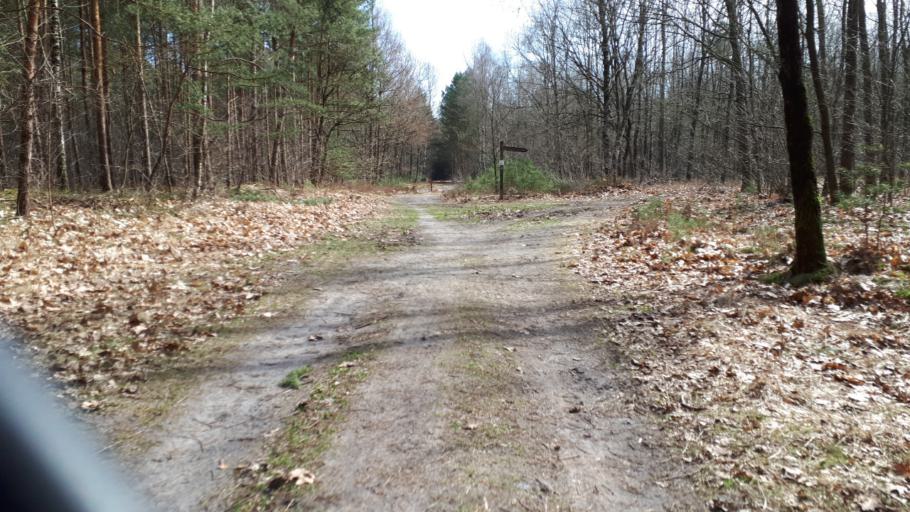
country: DE
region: Lower Saxony
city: Grossenkneten
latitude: 53.0208
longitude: 8.2965
